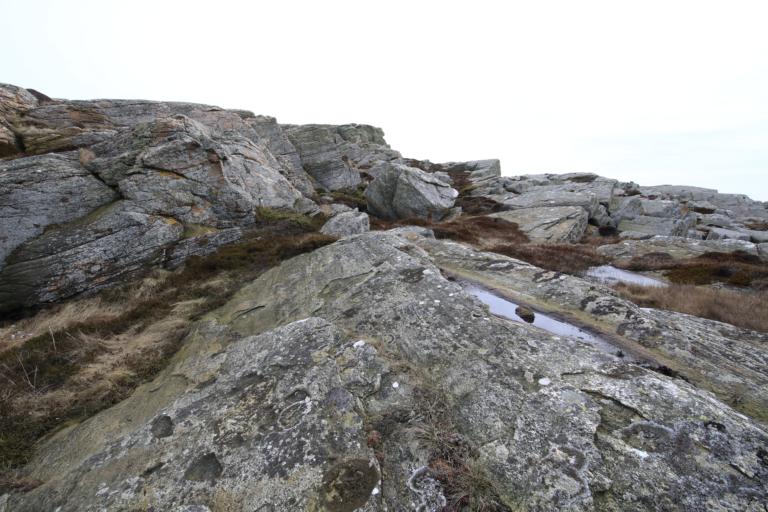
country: SE
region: Halland
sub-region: Kungsbacka Kommun
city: Frillesas
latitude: 57.2353
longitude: 12.0947
